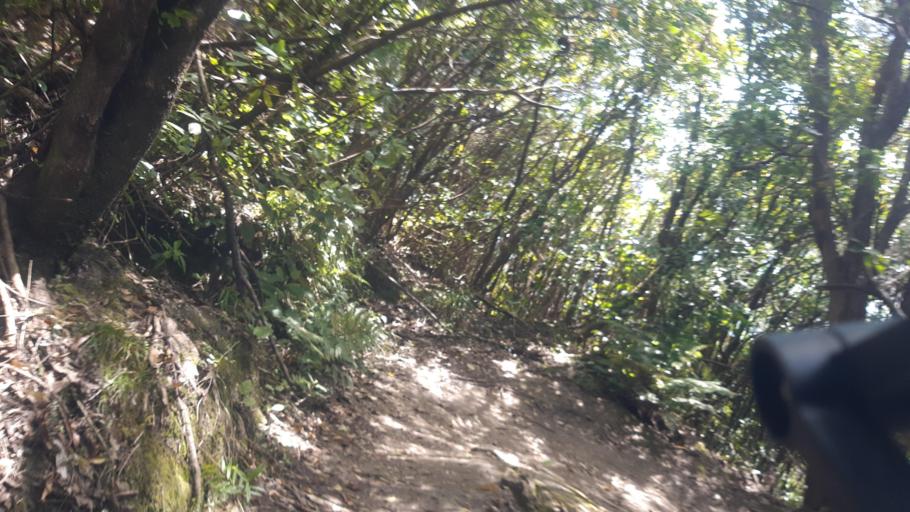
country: NZ
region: Marlborough
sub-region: Marlborough District
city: Picton
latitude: -41.2593
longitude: 174.0359
